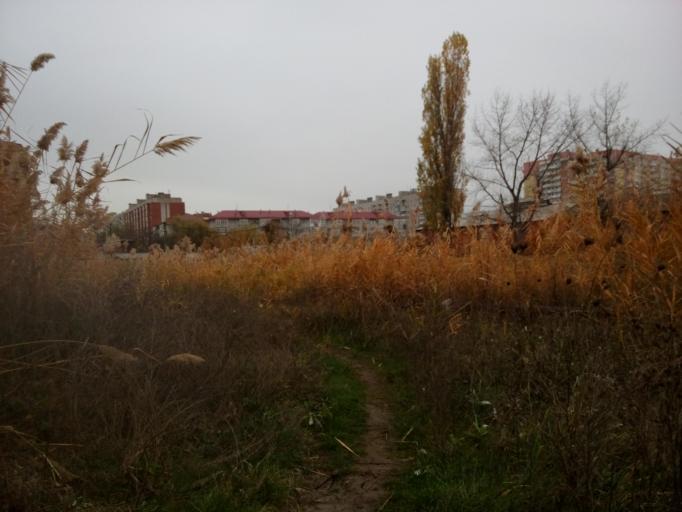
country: RU
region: Krasnodarskiy
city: Krasnodar
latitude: 45.0394
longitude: 39.0168
